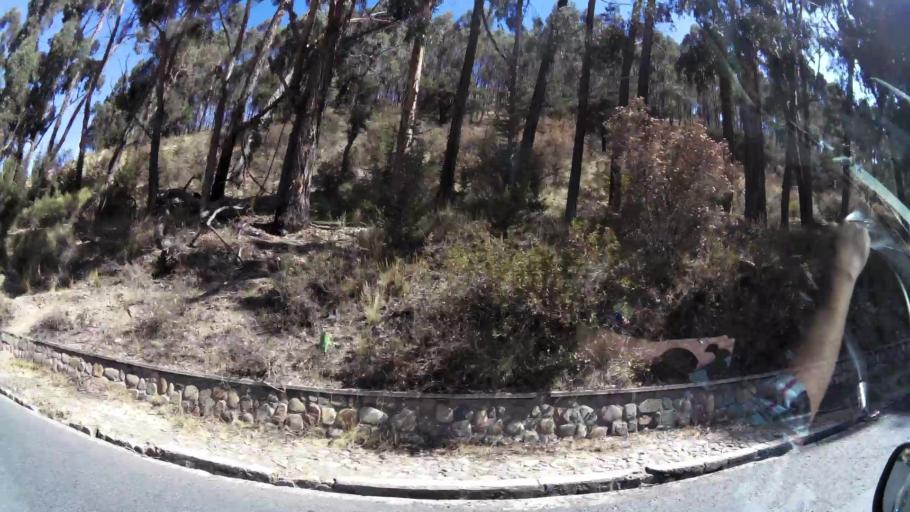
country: BO
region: La Paz
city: La Paz
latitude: -16.4833
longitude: -68.1552
